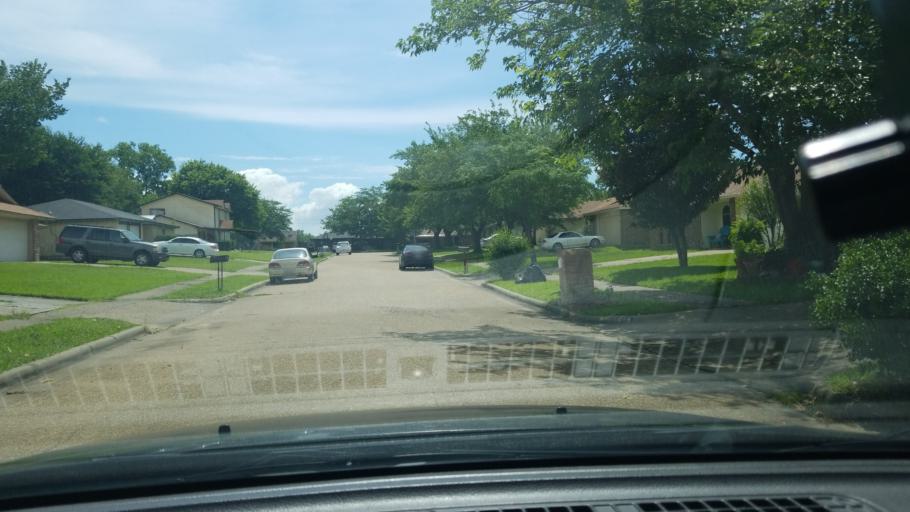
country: US
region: Texas
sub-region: Dallas County
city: Mesquite
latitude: 32.7557
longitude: -96.5769
